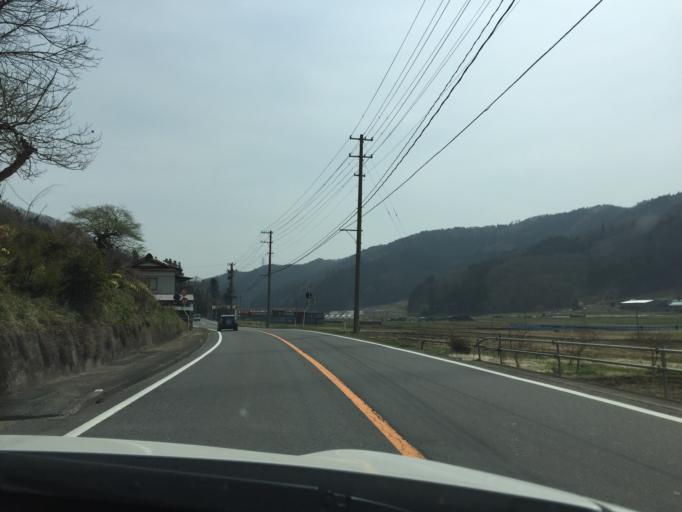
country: JP
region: Fukushima
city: Ishikawa
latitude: 37.1172
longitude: 140.5045
